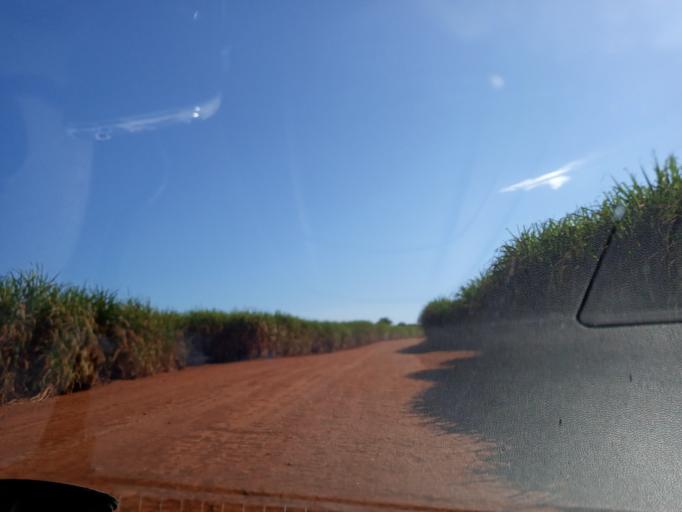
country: BR
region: Goias
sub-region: Itumbiara
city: Itumbiara
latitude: -18.4470
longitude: -49.1771
